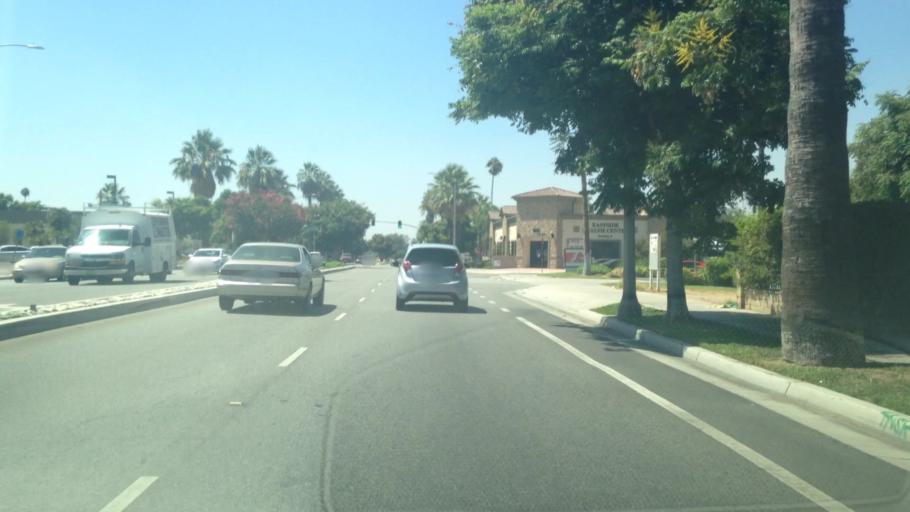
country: US
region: California
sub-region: Riverside County
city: Highgrove
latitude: 33.9757
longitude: -117.3532
